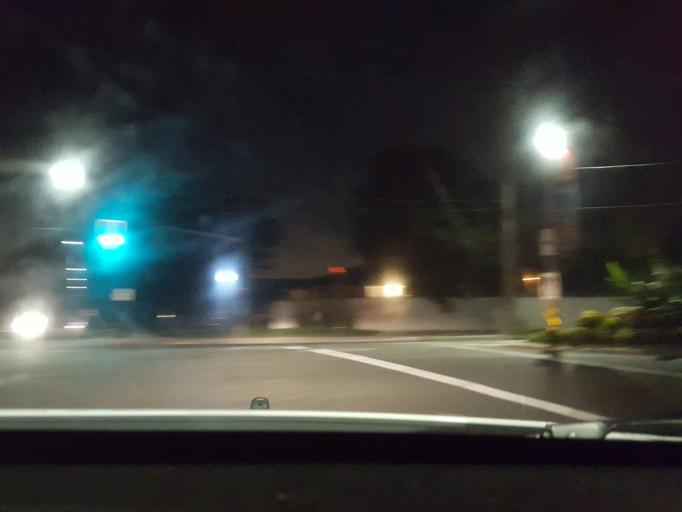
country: CA
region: Ontario
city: Hamilton
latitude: 43.2210
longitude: -79.8901
